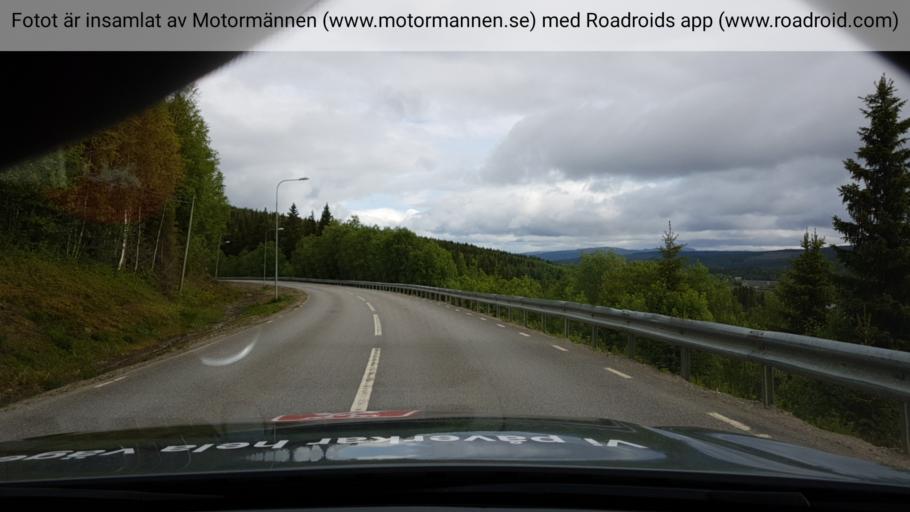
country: NO
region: Nord-Trondelag
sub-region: Lierne
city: Sandvika
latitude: 64.4867
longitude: 14.1359
